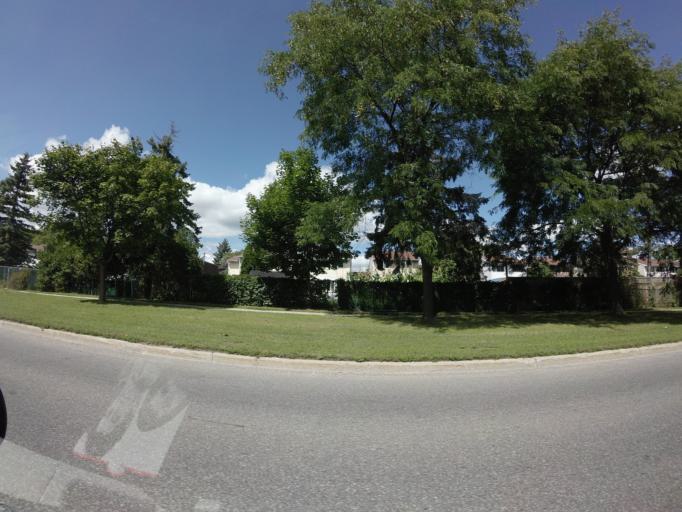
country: CA
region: Quebec
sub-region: Outaouais
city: Gatineau
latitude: 45.4772
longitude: -75.5458
